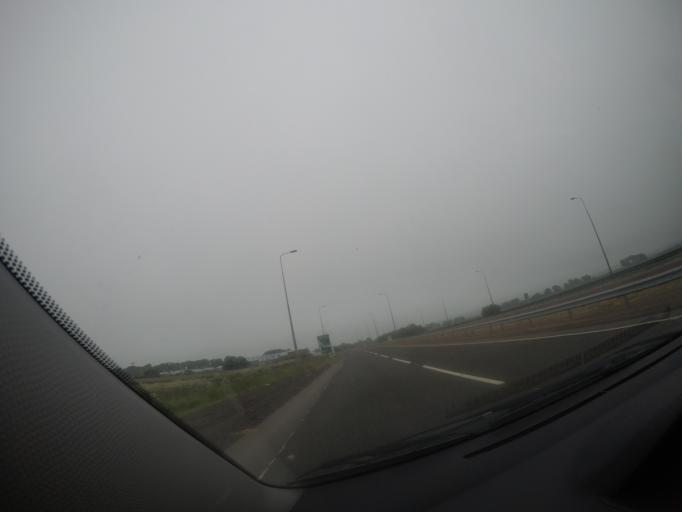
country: GB
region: Scotland
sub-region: Angus
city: Forfar
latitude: 56.5722
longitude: -2.9165
